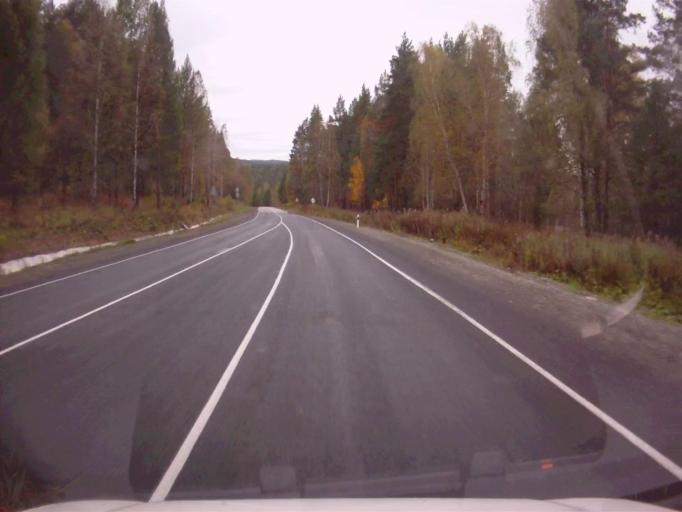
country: RU
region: Chelyabinsk
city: Nyazepetrovsk
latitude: 56.0621
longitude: 59.7280
